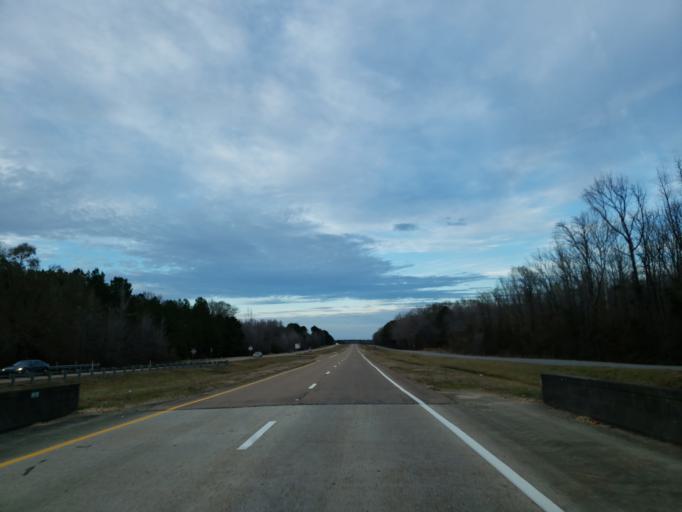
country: US
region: Mississippi
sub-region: Lauderdale County
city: Meridian Station
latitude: 32.5298
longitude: -88.5120
